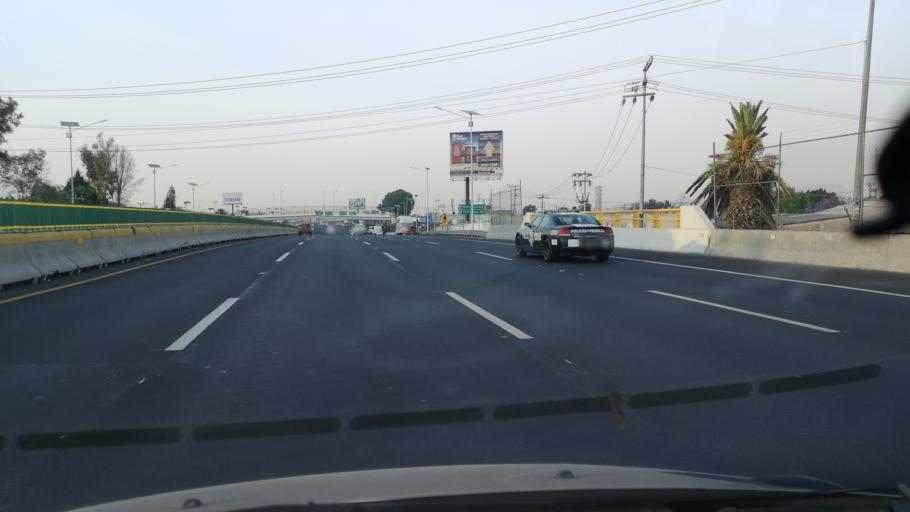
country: MX
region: Mexico
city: Ecatepec
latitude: 19.5939
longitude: -99.0405
